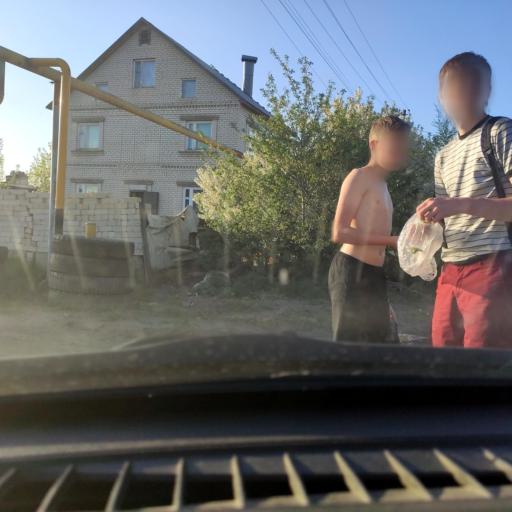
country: RU
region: Samara
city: Tol'yatti
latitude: 53.5631
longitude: 49.4087
